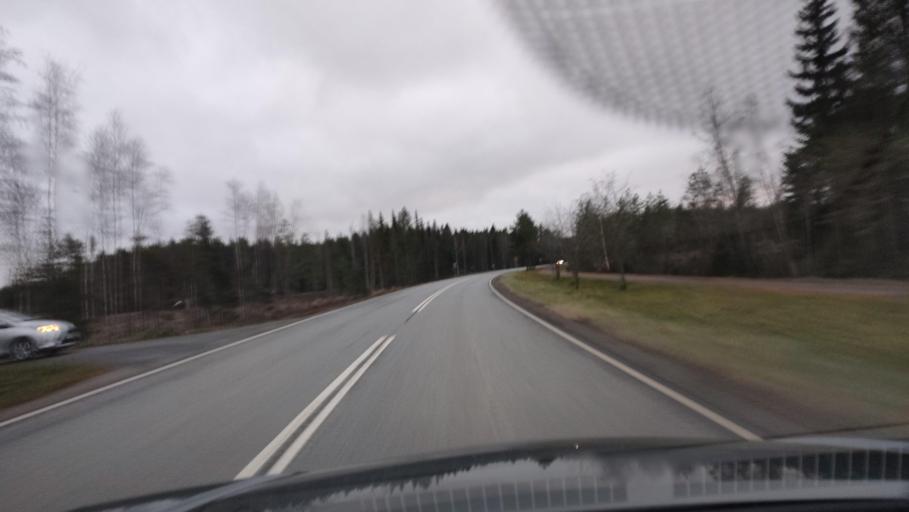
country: FI
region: Southern Ostrobothnia
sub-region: Suupohja
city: Kauhajoki
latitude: 62.3952
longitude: 22.1561
